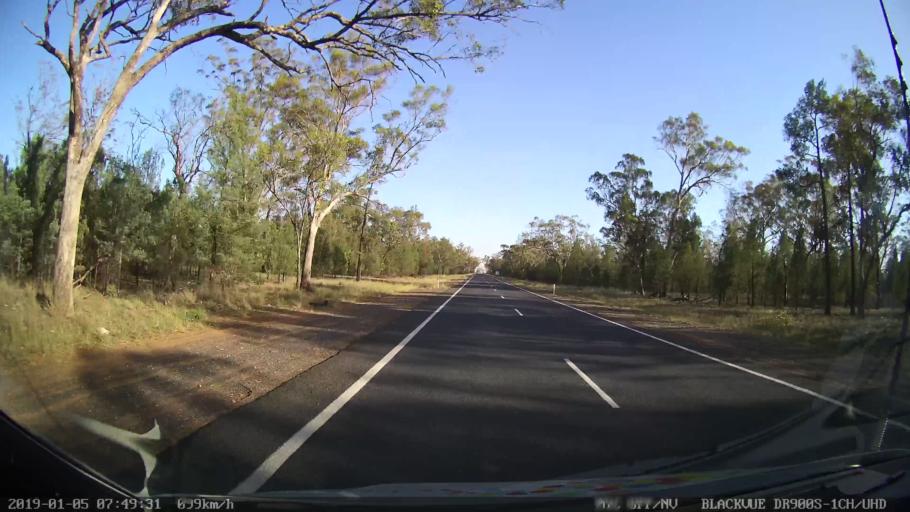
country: AU
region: New South Wales
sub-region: Gilgandra
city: Gilgandra
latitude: -31.8006
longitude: 148.6362
